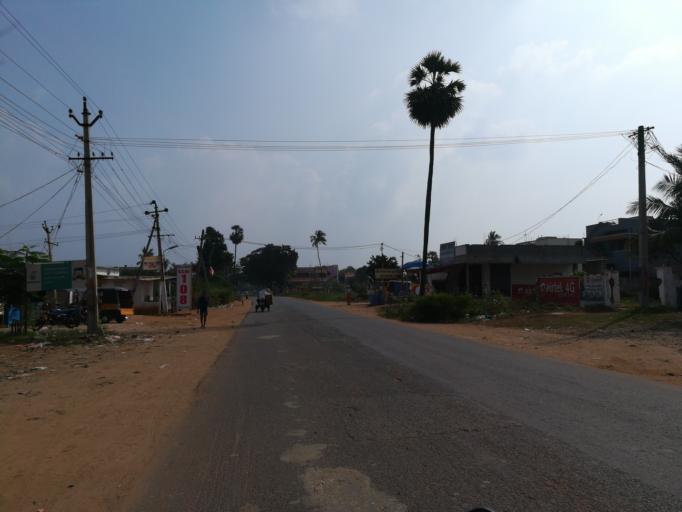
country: IN
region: Andhra Pradesh
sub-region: Nellore
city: Kovur
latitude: 14.5528
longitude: 79.9902
